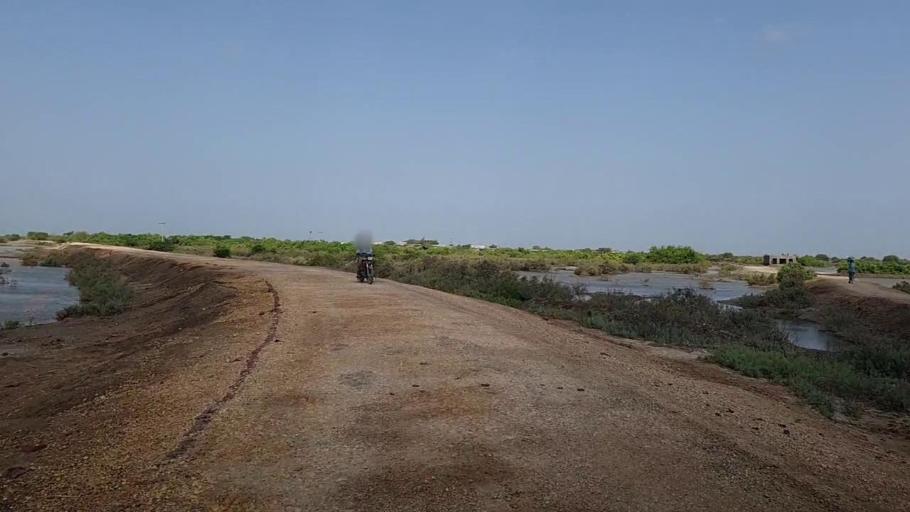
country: PK
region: Sindh
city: Mirpur Batoro
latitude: 24.6460
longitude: 68.4304
